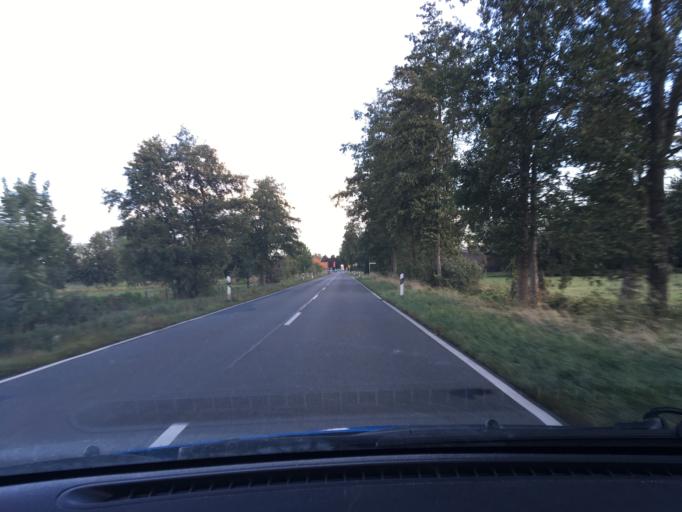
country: DE
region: Lower Saxony
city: Bleckede
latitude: 53.3003
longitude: 10.7107
